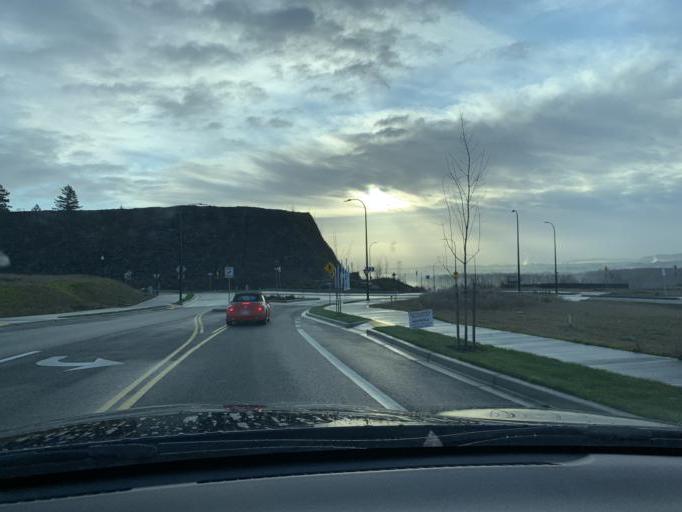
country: US
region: Washington
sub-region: Clark County
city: Mill Plain
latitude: 45.5866
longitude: -122.4715
